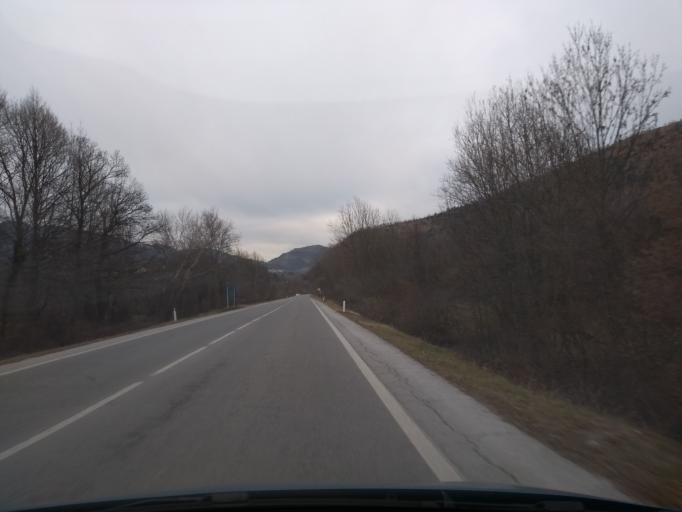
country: IT
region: Piedmont
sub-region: Provincia di Torino
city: Germagnano
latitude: 45.2596
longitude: 7.4714
